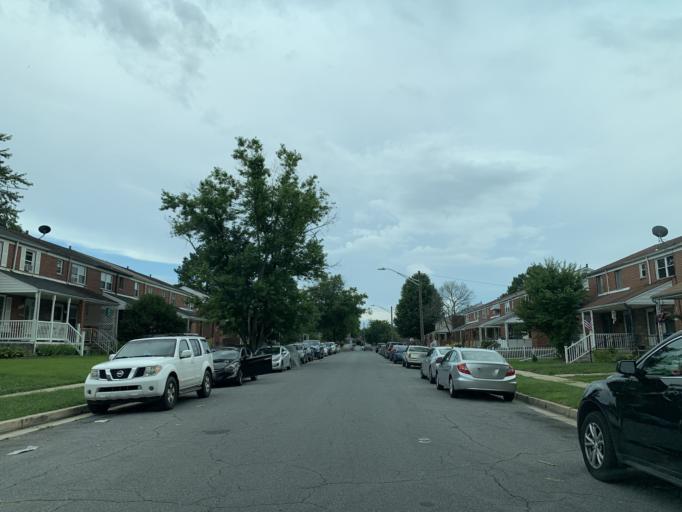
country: US
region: Maryland
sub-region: Baltimore County
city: Essex
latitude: 39.2979
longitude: -76.4514
